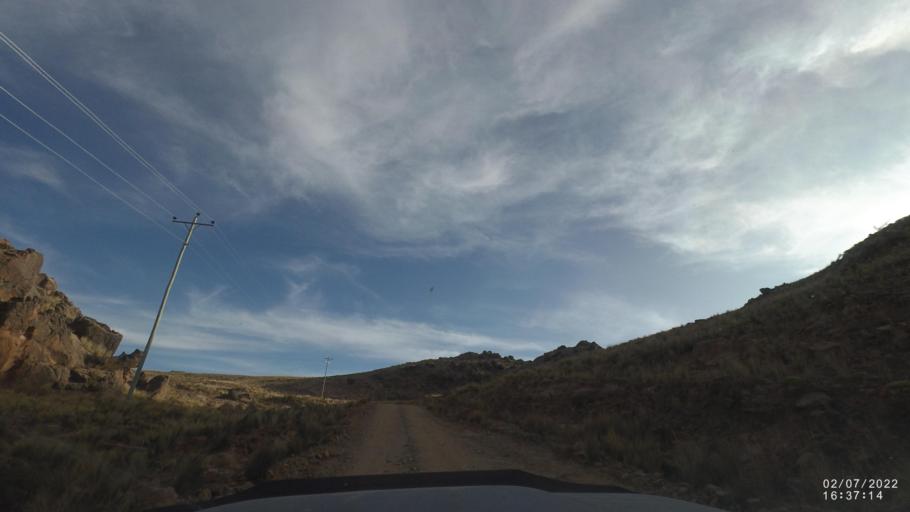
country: BO
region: Cochabamba
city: Irpa Irpa
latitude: -17.9660
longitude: -66.4969
